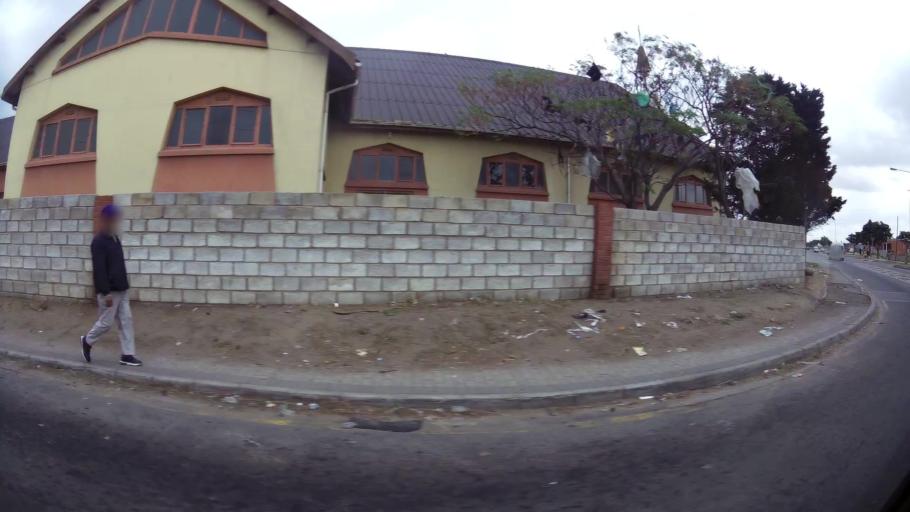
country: ZA
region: Eastern Cape
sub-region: Nelson Mandela Bay Metropolitan Municipality
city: Port Elizabeth
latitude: -33.8814
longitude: 25.5965
